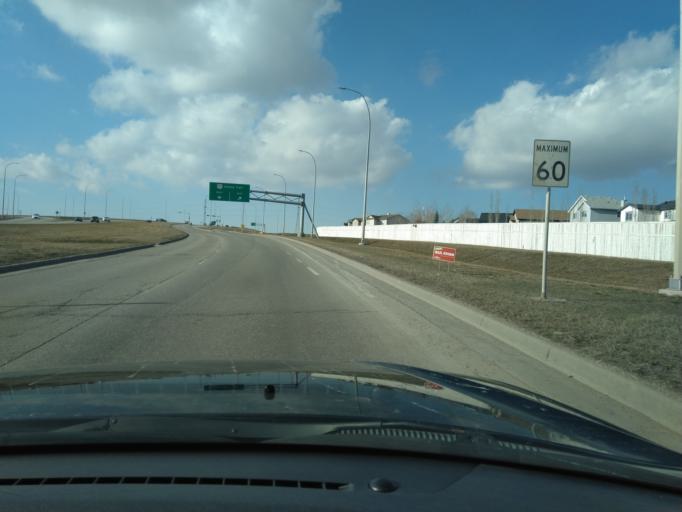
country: CA
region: Alberta
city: Calgary
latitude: 51.1688
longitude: -114.0677
